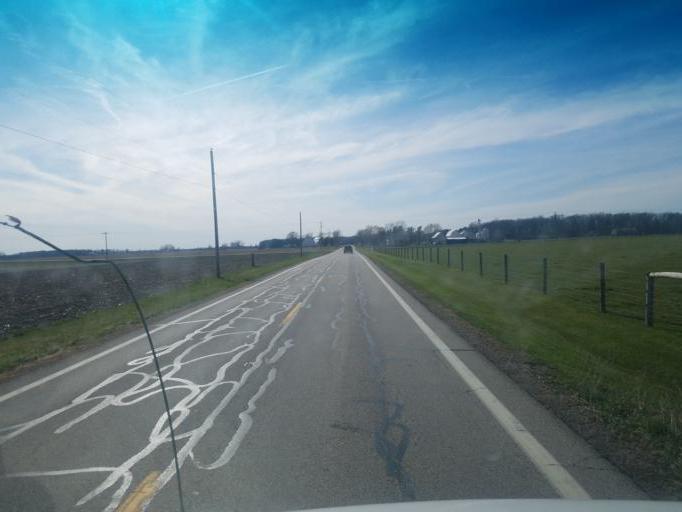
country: US
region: Ohio
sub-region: Union County
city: Richwood
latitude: 40.3512
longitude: -83.3509
